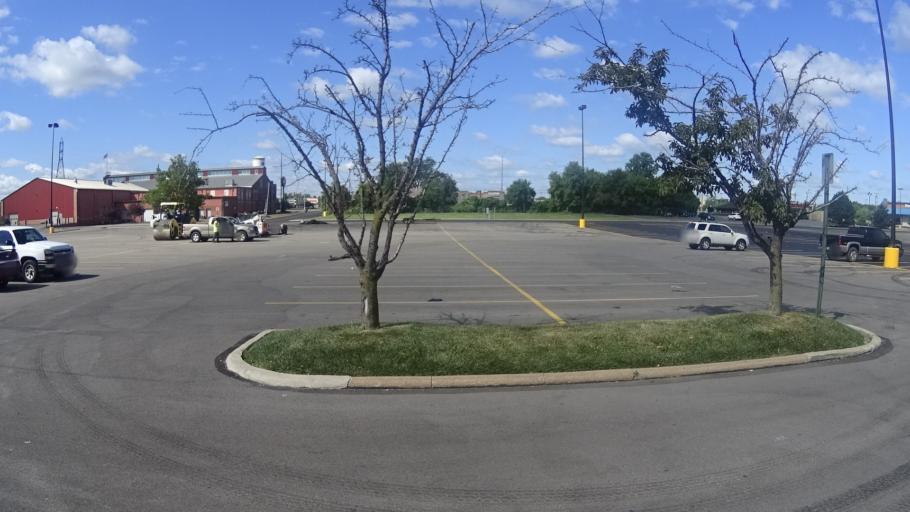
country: US
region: Ohio
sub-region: Erie County
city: Sandusky
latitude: 41.4060
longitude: -82.6587
